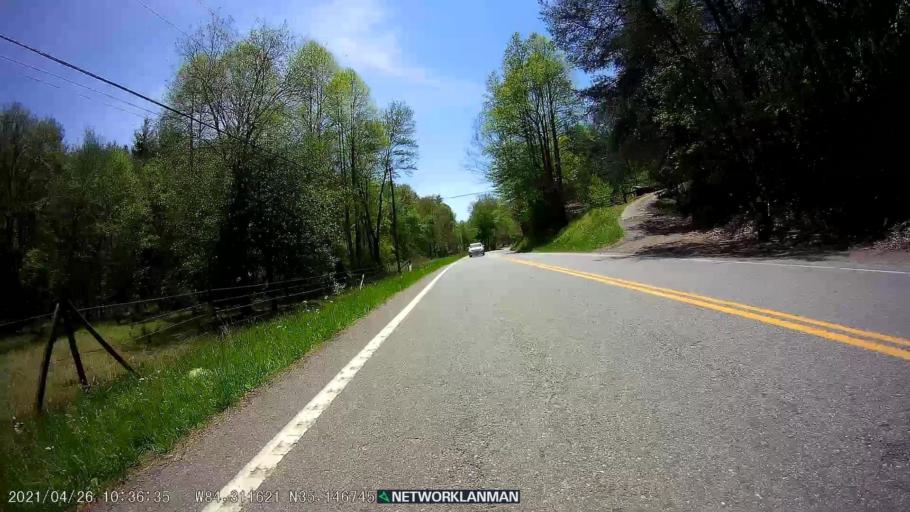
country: US
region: Georgia
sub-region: Fannin County
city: McCaysville
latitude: 35.1468
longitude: -84.3116
